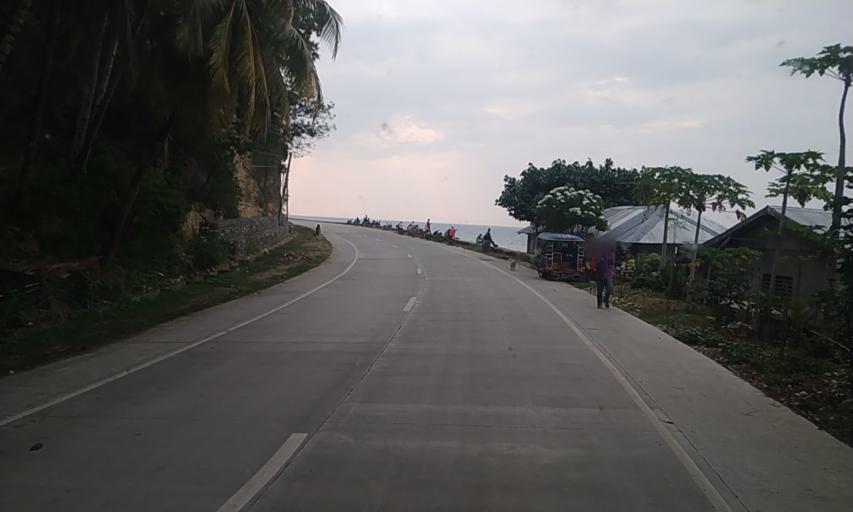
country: PH
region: Central Visayas
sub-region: Province of Negros Oriental
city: Calamba
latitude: 10.1904
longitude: 123.2922
